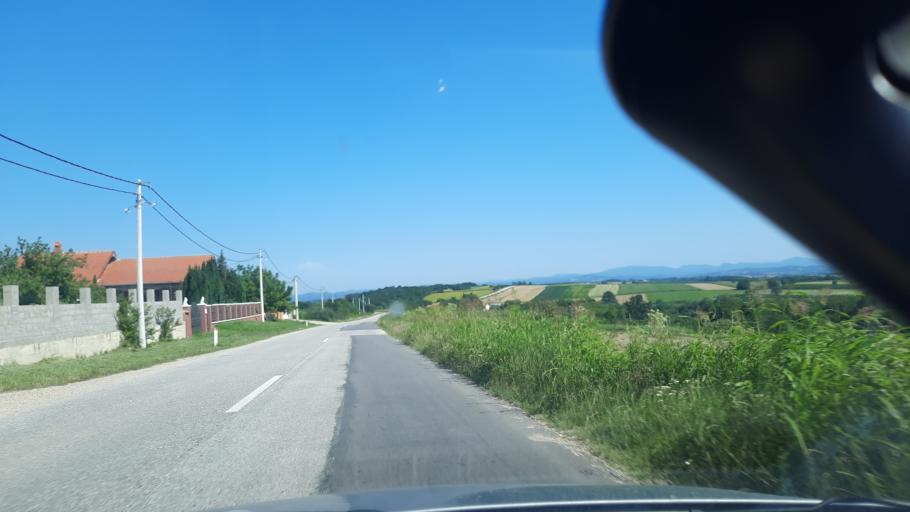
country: RS
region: Central Serbia
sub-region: Branicevski Okrug
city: Malo Crnice
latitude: 44.5842
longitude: 21.4112
